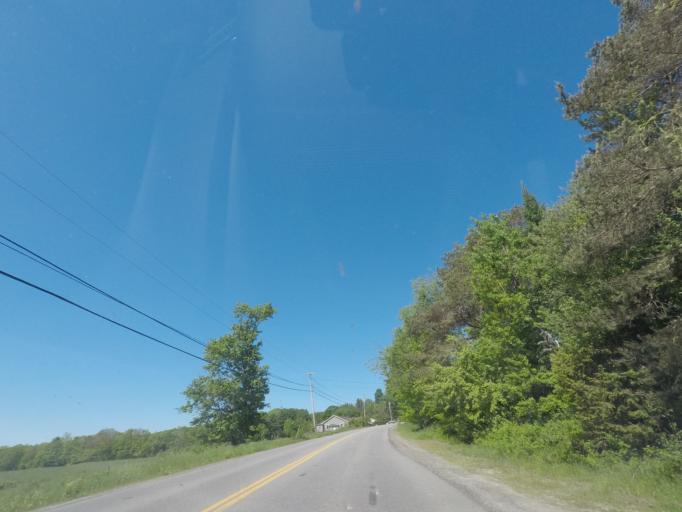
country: US
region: Maine
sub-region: Kennebec County
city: Gardiner
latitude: 44.2314
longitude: -69.7914
